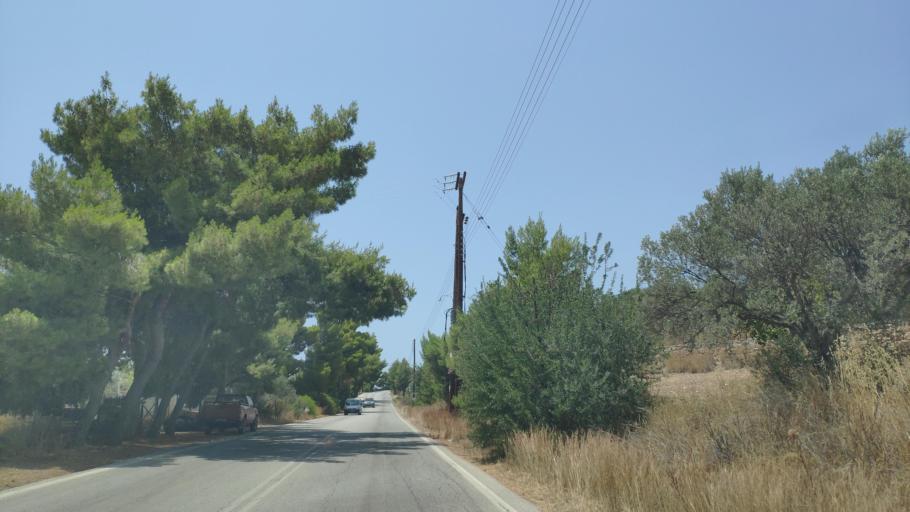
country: GR
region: Peloponnese
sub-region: Nomos Argolidos
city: Kranidi
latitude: 37.3727
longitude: 23.1555
